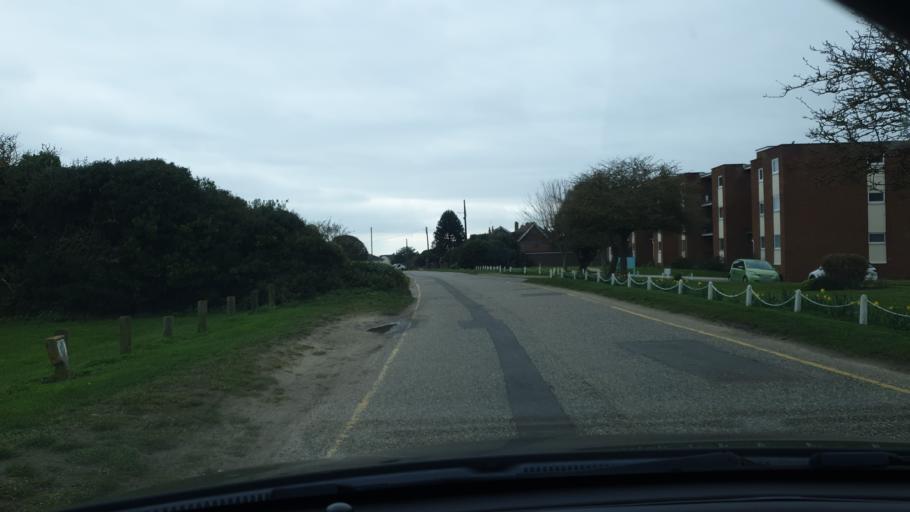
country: GB
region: England
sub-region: Essex
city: Walton-on-the-Naze
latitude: 51.8629
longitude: 1.2856
